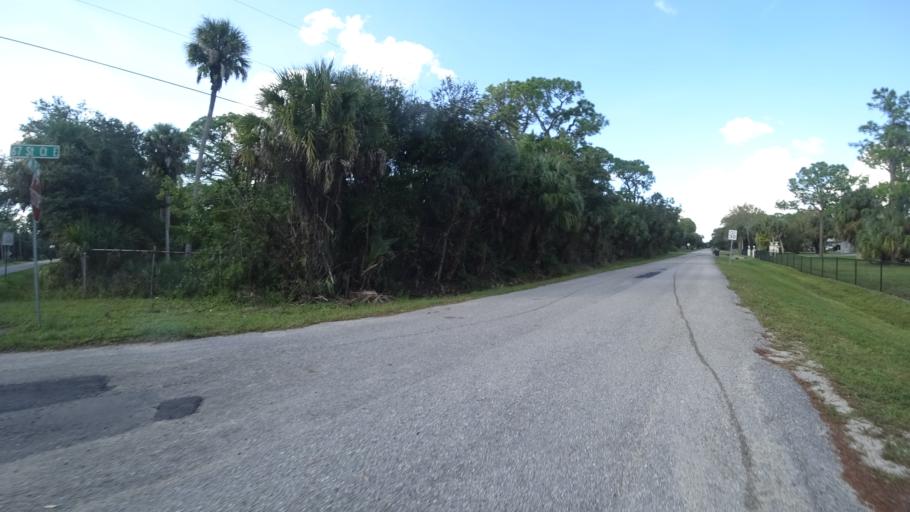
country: US
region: Florida
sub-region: Manatee County
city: Ellenton
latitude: 27.4830
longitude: -82.4754
